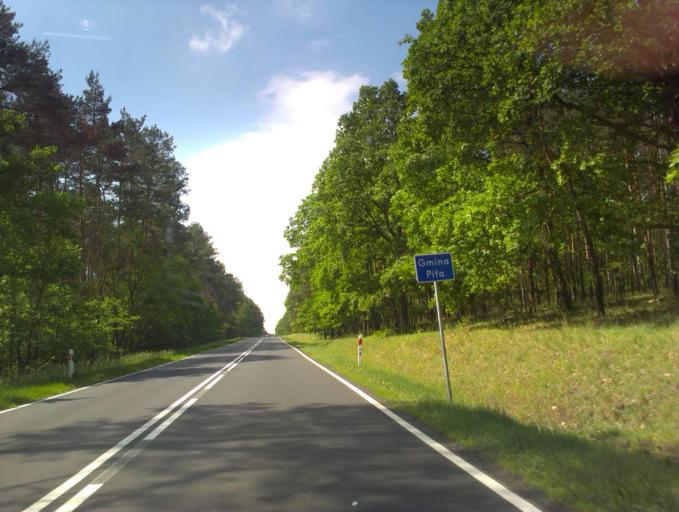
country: PL
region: Greater Poland Voivodeship
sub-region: Powiat pilski
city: Pila
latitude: 53.1953
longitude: 16.7724
